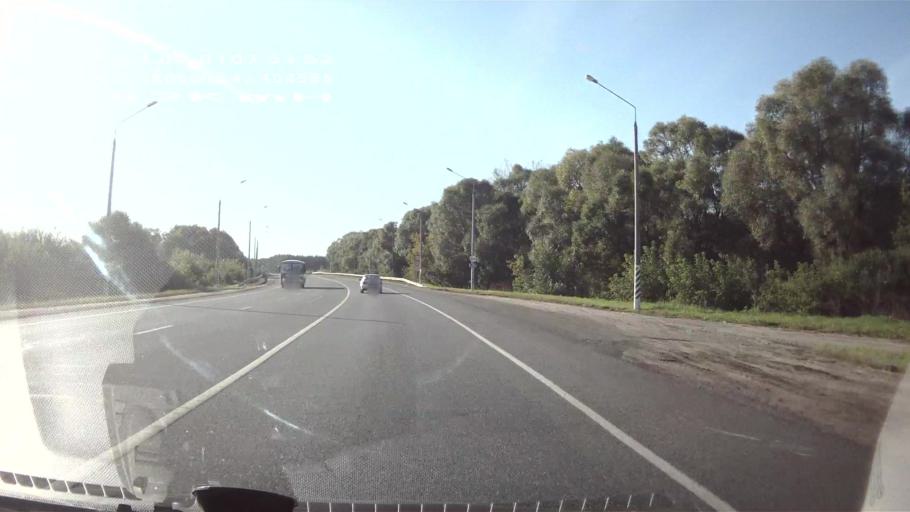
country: RU
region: Chuvashia
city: Shikhazany
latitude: 55.5601
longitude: 47.4049
